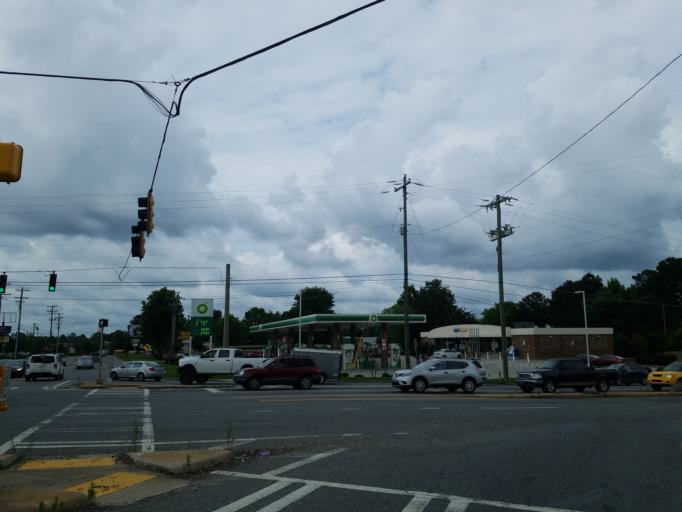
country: US
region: Georgia
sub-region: Fulton County
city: Milton
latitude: 34.1361
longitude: -84.2489
